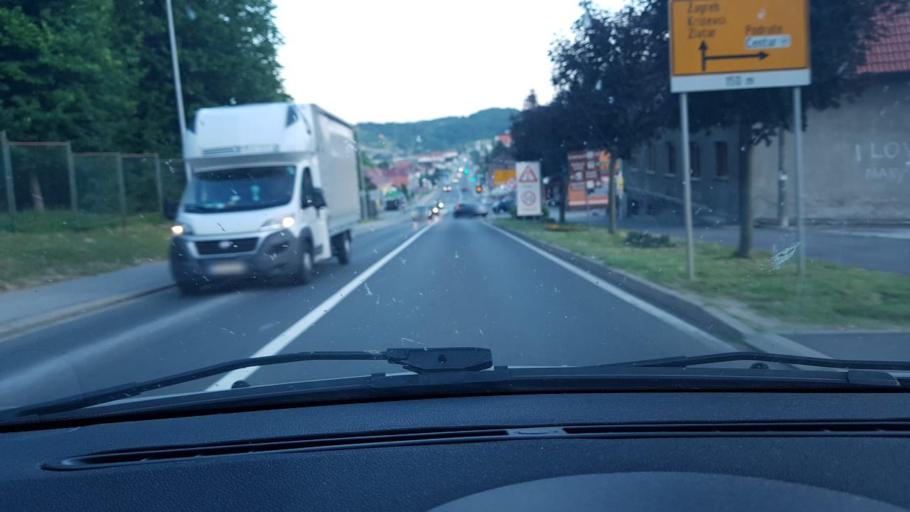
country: HR
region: Varazdinska
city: Remetinec
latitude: 46.1661
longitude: 16.3350
